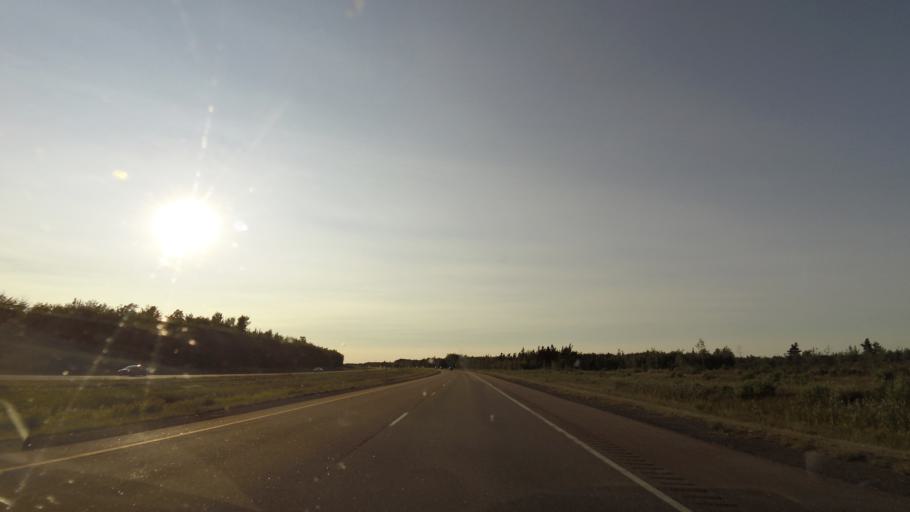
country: CA
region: New Brunswick
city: Dieppe
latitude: 46.1268
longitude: -64.6419
